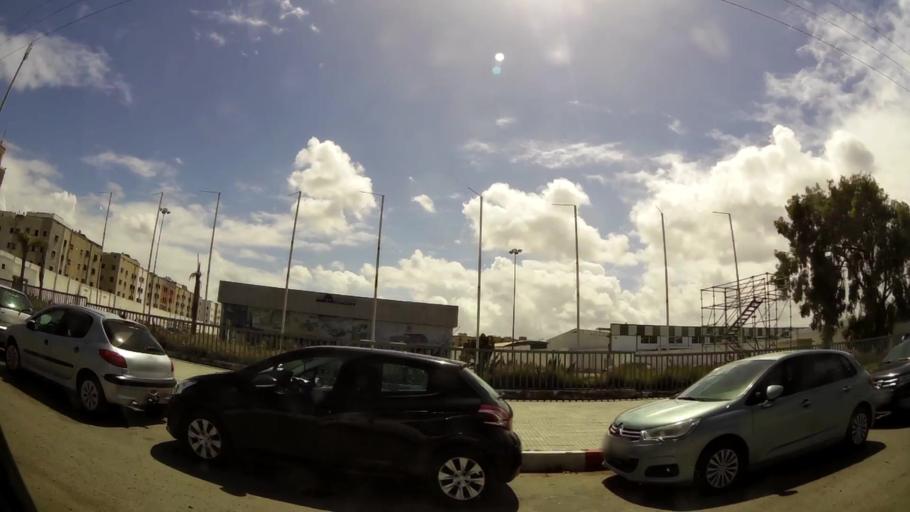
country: MA
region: Grand Casablanca
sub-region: Mediouna
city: Tit Mellil
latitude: 33.5978
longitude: -7.4960
